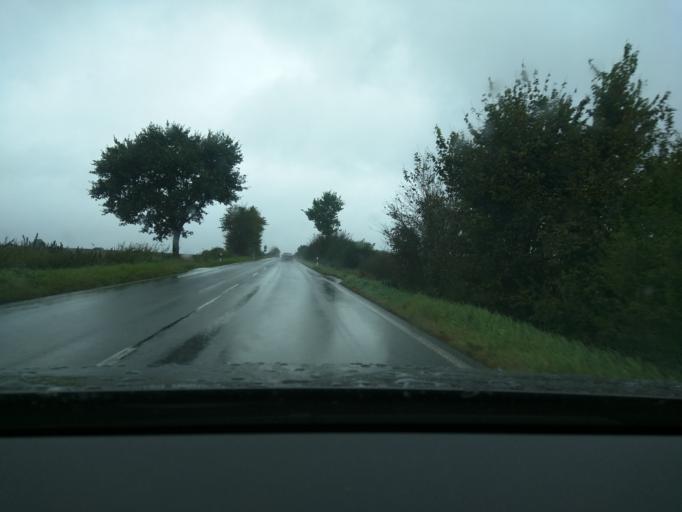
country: DE
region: Schleswig-Holstein
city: Wangelau
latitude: 53.4466
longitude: 10.5580
